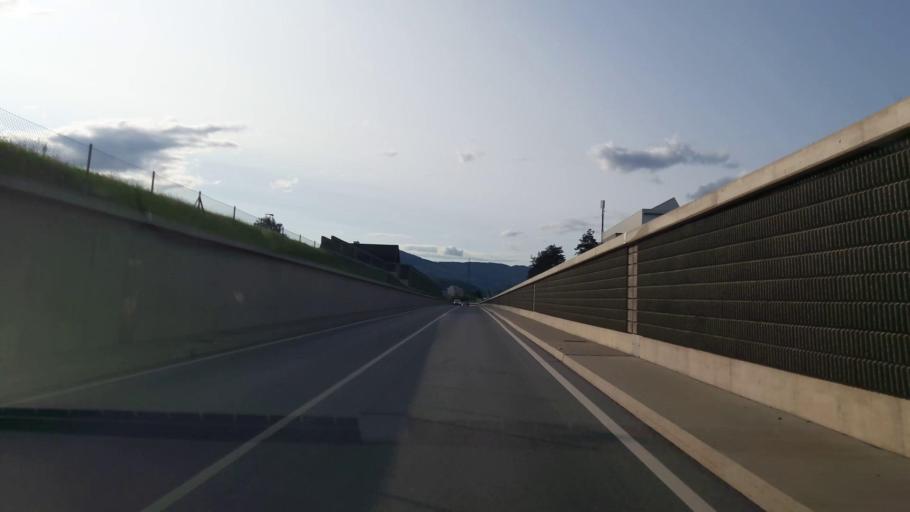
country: AT
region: Styria
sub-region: Politischer Bezirk Weiz
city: Krottendorf
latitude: 47.2027
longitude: 15.6459
